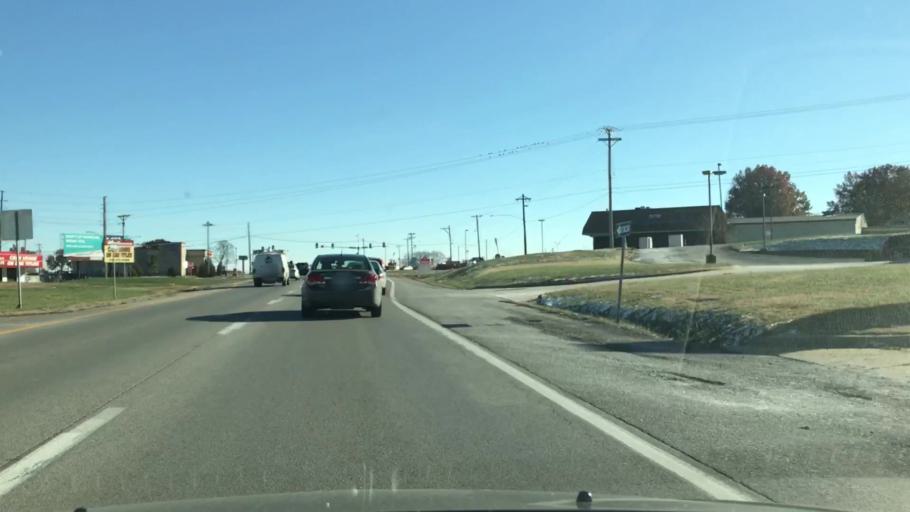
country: US
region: Missouri
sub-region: Jackson County
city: Raytown
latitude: 38.9878
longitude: -94.4656
